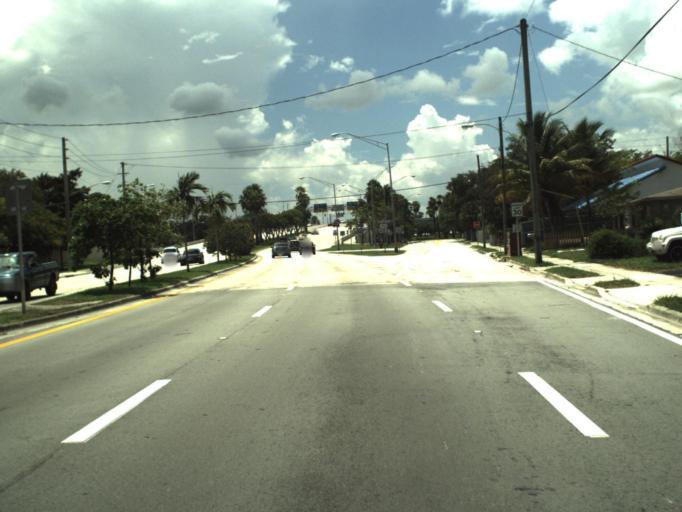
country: US
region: Florida
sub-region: Broward County
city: Boulevard Gardens
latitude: 26.1072
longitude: -80.1636
